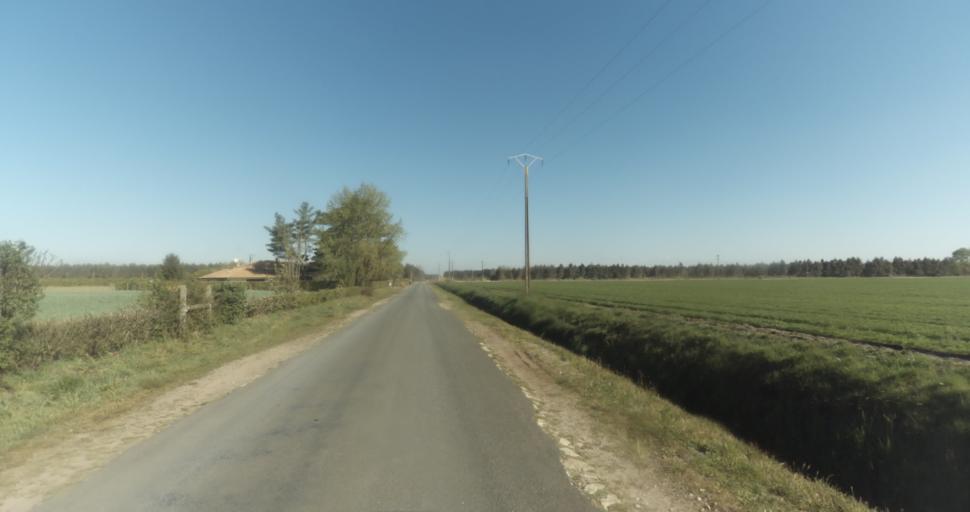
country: FR
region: Aquitaine
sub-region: Departement de la Gironde
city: Marcheprime
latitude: 44.7733
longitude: -0.8578
